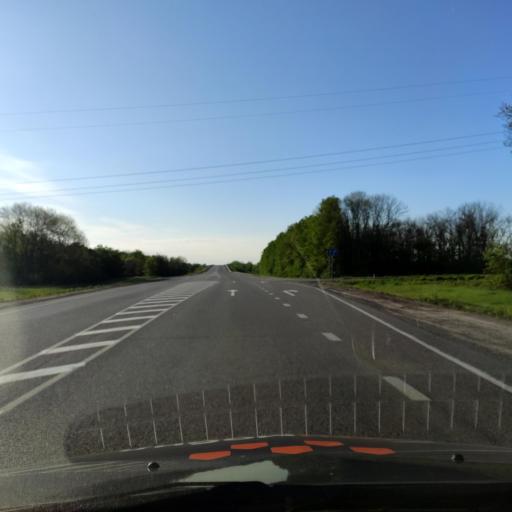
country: RU
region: Lipetsk
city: Yelets
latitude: 52.5671
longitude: 38.6702
